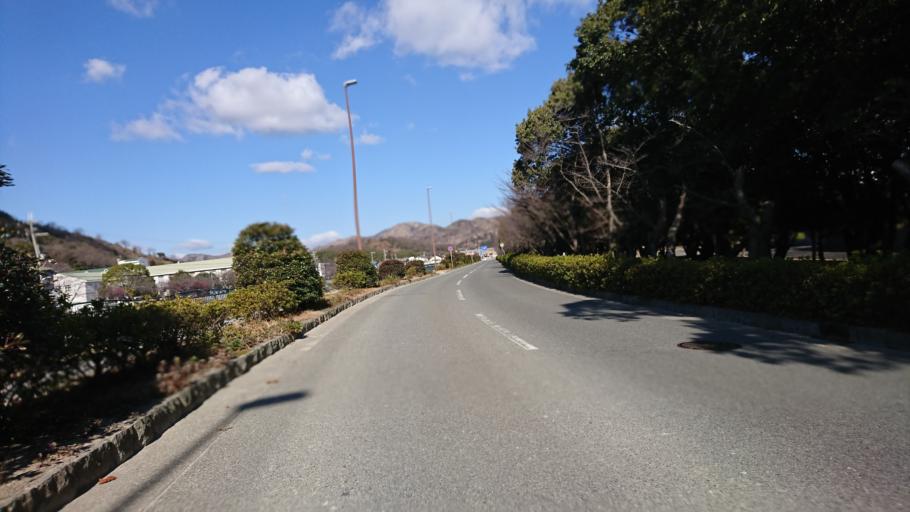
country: JP
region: Hyogo
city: Kakogawacho-honmachi
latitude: 34.7802
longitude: 134.7979
